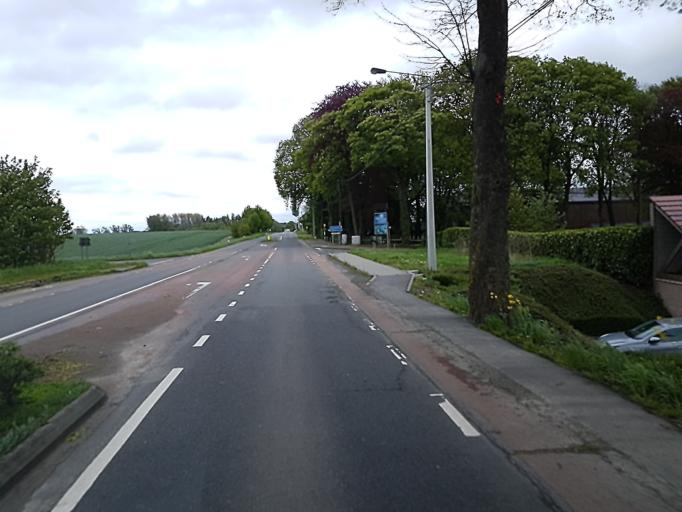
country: BE
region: Wallonia
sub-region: Province de Namur
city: Gembloux
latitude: 50.5899
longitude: 4.7201
